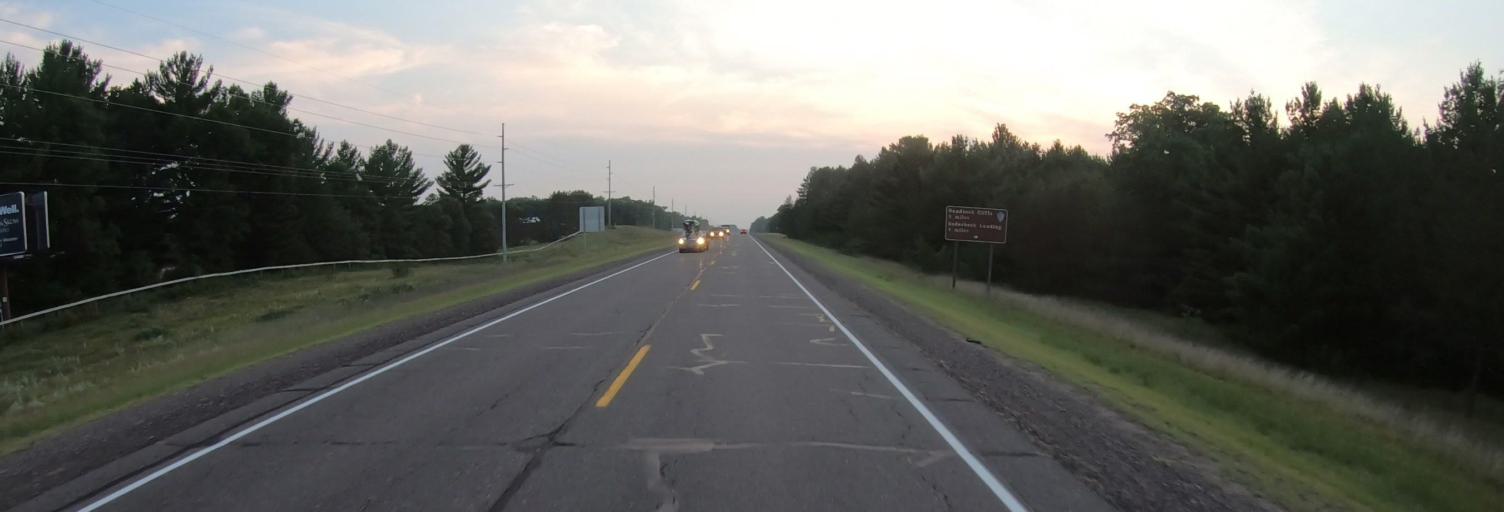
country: US
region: Wisconsin
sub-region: Burnett County
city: Grantsburg
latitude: 45.7731
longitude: -92.7397
